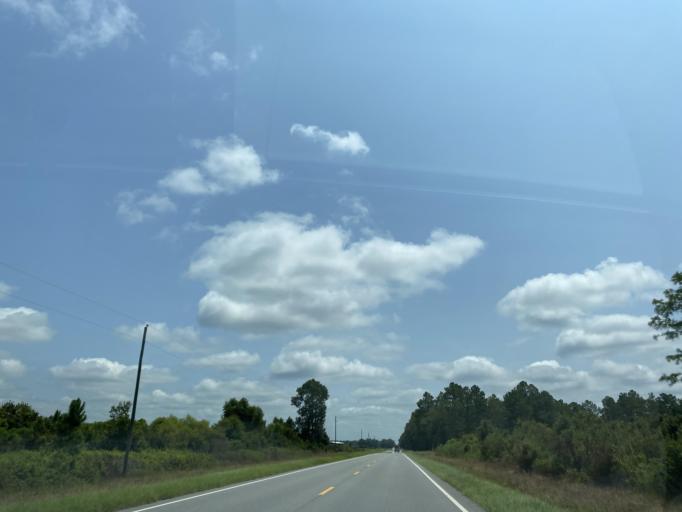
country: US
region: Georgia
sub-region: Jeff Davis County
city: Hazlehurst
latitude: 31.7278
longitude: -82.5305
